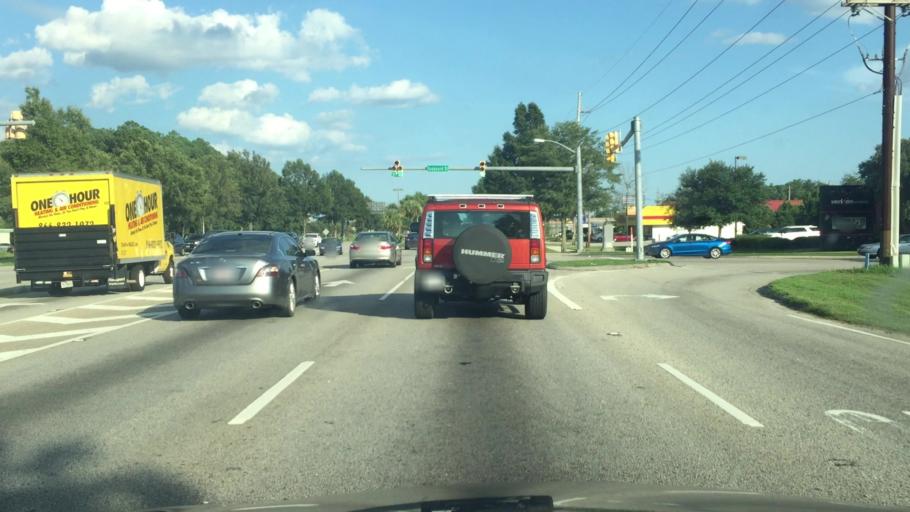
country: US
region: South Carolina
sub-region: Horry County
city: Myrtle Beach
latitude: 33.7067
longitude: -78.9111
